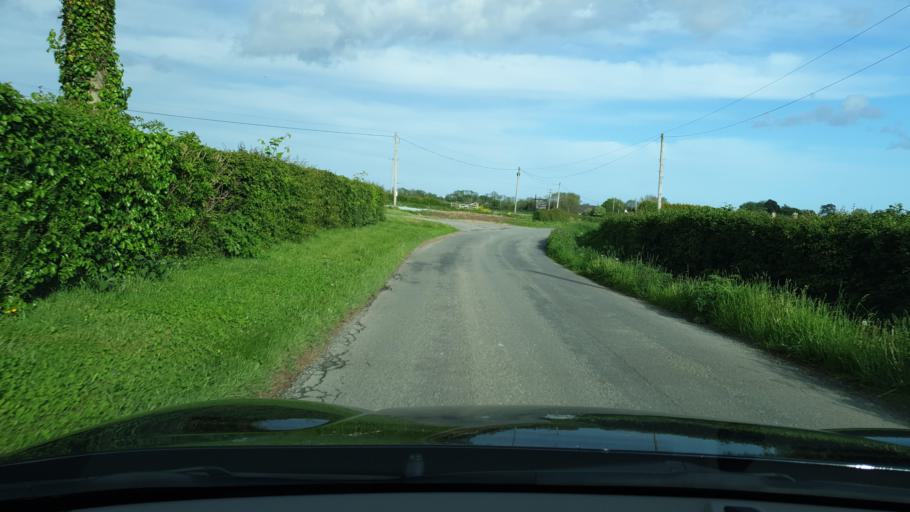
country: IE
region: Leinster
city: Lusk
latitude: 53.5430
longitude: -6.1985
